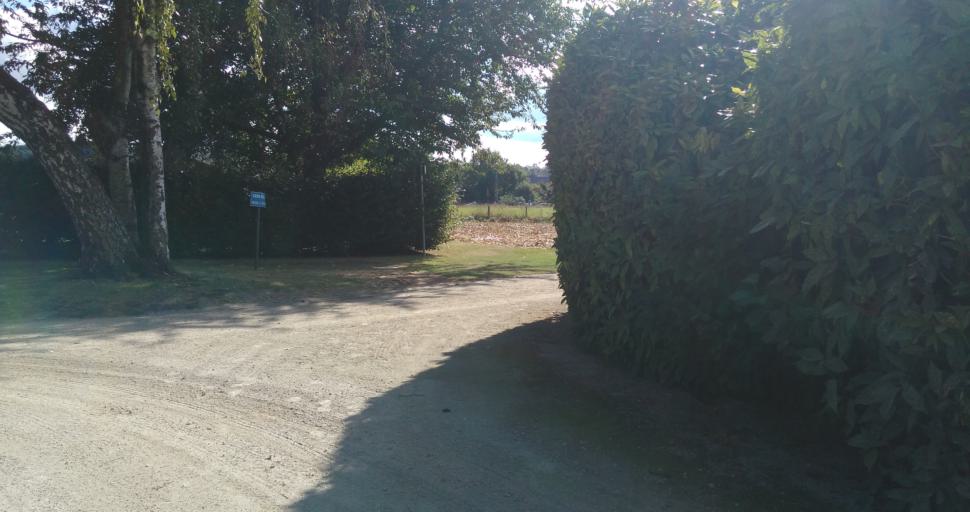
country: BE
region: Flanders
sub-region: Provincie Vlaams-Brabant
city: Herent
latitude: 50.9004
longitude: 4.6417
